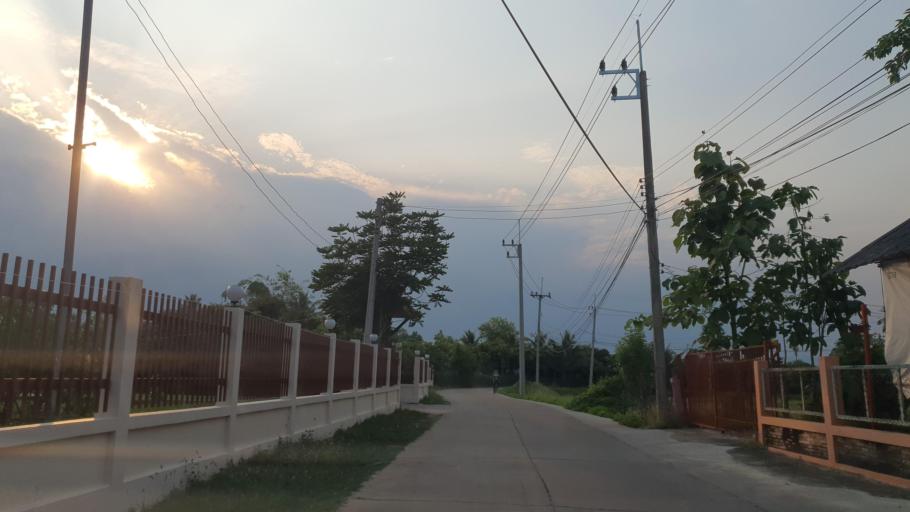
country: TH
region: Chiang Mai
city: Hang Dong
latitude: 18.6608
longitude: 98.9352
